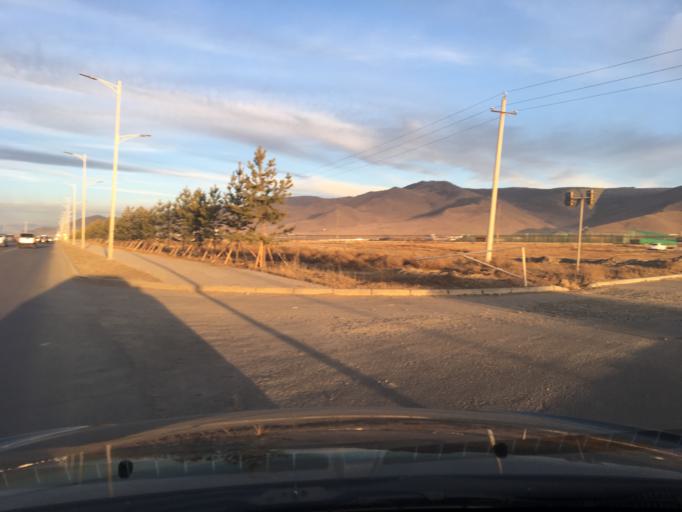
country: MN
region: Ulaanbaatar
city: Ulaanbaatar
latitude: 47.8639
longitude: 106.8071
